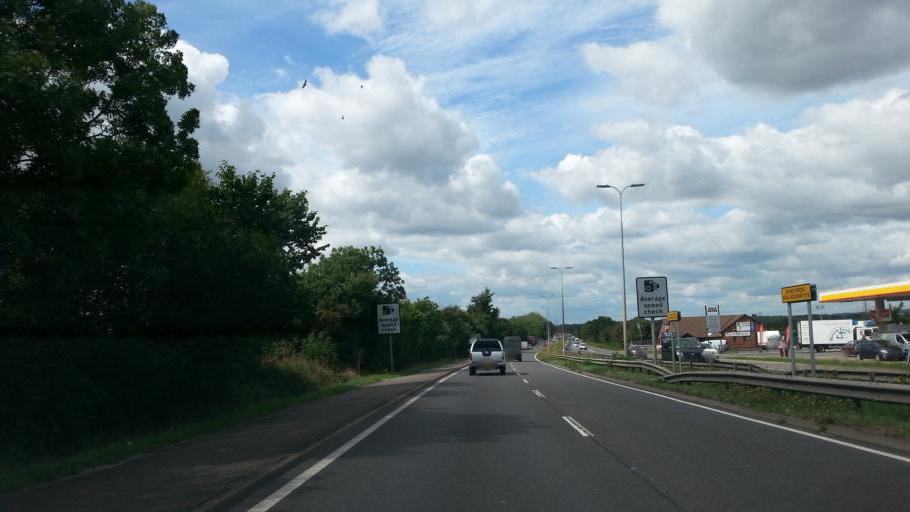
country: GB
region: England
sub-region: Essex
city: Wickford
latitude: 51.5903
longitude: 0.5206
